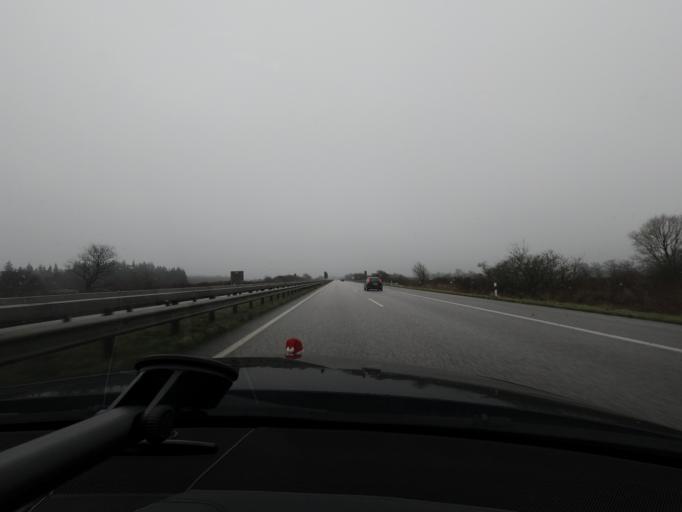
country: DE
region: Schleswig-Holstein
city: Bollingstedt
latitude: 54.6273
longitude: 9.4408
